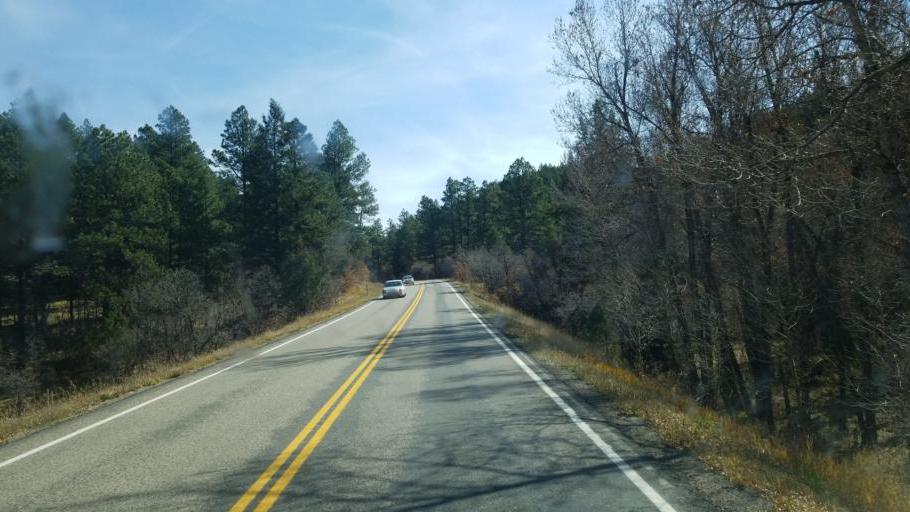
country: US
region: New Mexico
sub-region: Rio Arriba County
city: Dulce
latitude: 37.0756
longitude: -106.8480
